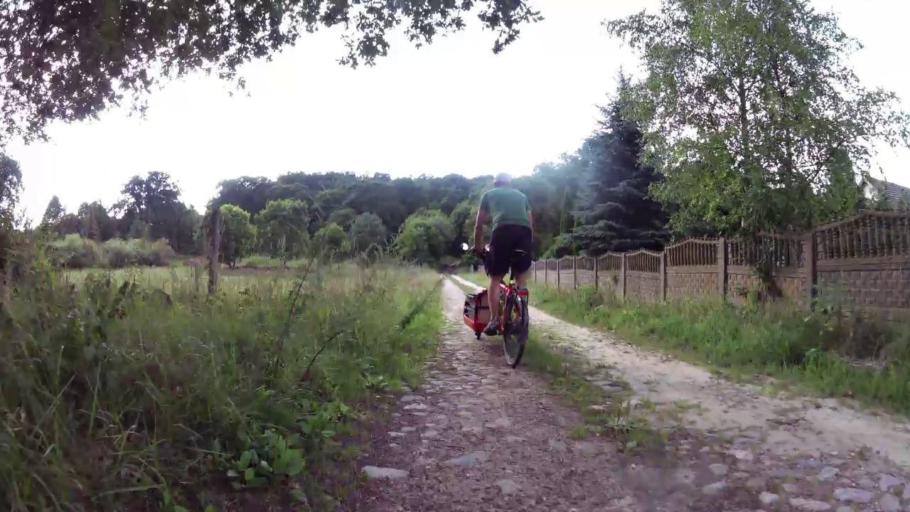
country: PL
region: West Pomeranian Voivodeship
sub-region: Powiat stargardzki
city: Insko
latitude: 53.4459
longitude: 15.6483
